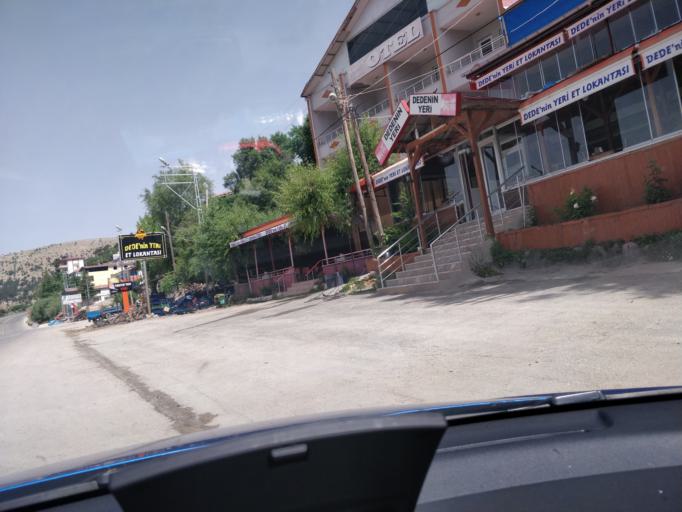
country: TR
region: Karaman
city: Bucakkisla
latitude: 36.8847
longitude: 33.2798
